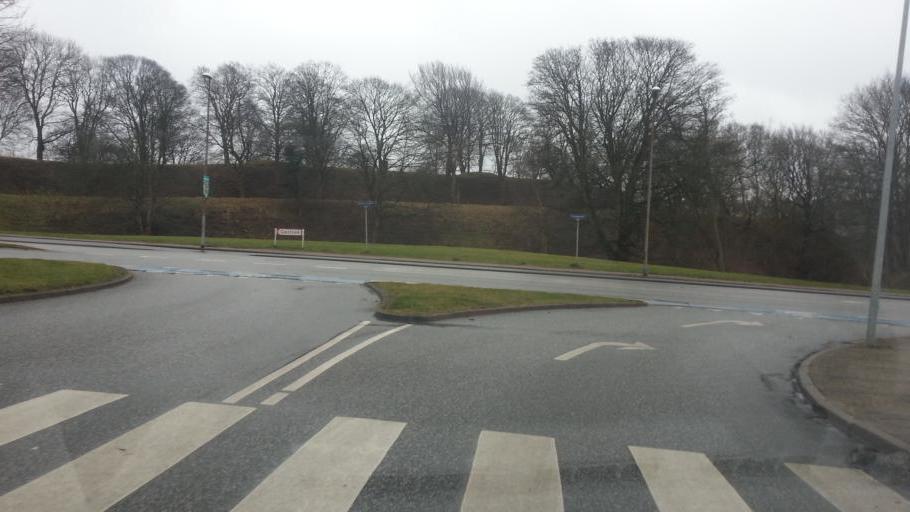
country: DK
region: South Denmark
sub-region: Fredericia Kommune
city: Fredericia
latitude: 55.5643
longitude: 9.7465
